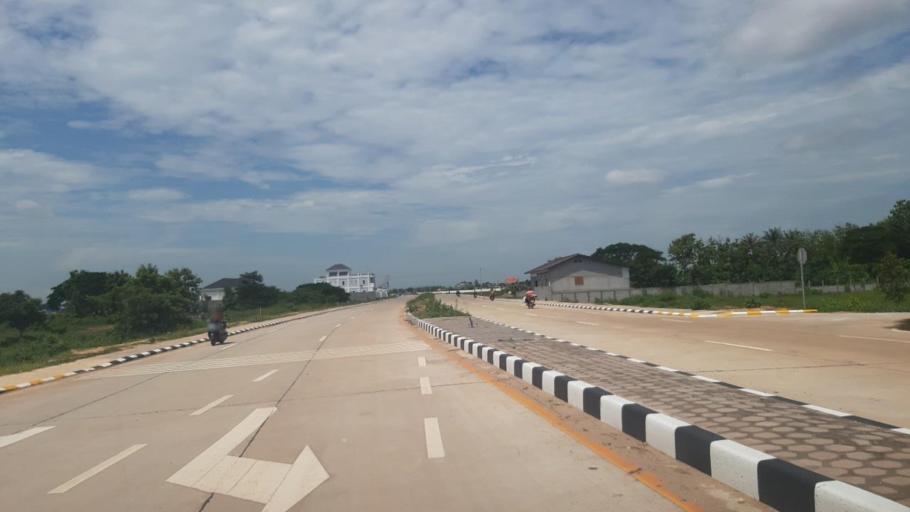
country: LA
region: Vientiane
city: Vientiane
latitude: 18.0388
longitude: 102.6145
